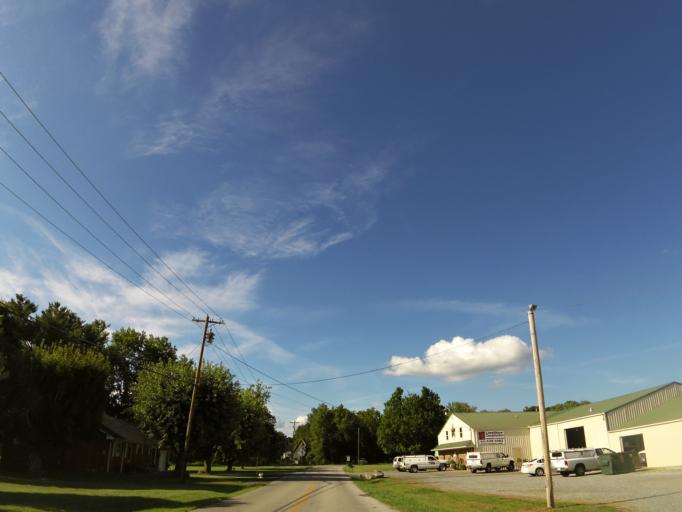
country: US
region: Tennessee
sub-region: Greene County
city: Tusculum
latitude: 36.1884
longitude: -82.7360
